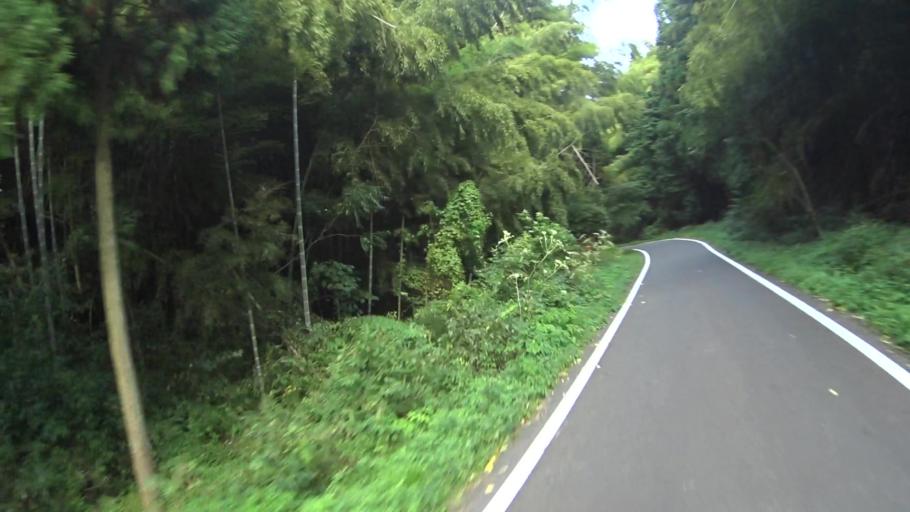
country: JP
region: Kyoto
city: Miyazu
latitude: 35.5650
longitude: 135.1294
